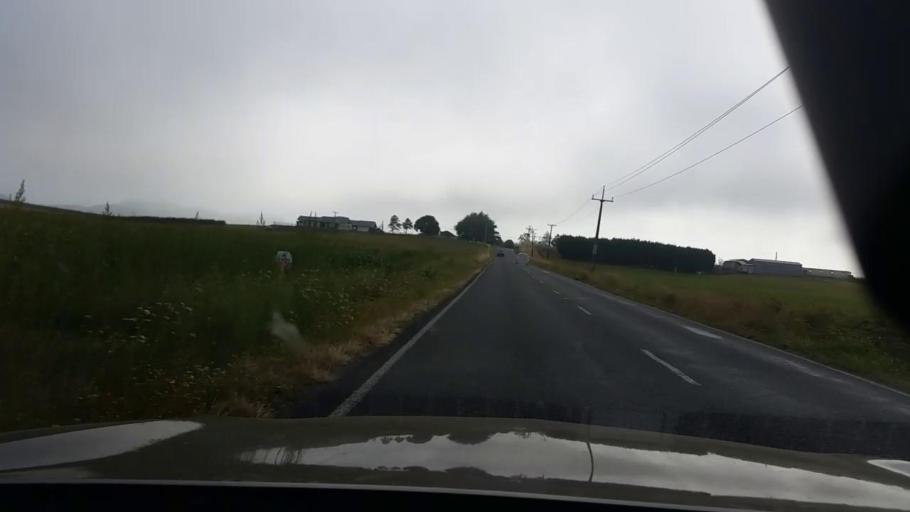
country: NZ
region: Waikato
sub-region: Hamilton City
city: Hamilton
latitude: -37.6225
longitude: 175.3295
